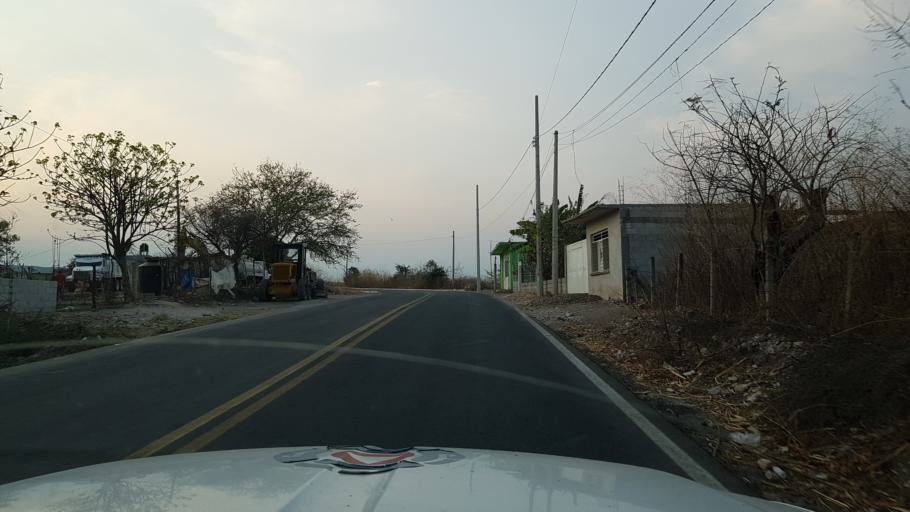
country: MX
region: Morelos
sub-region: Ayala
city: Olintepec
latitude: 18.7323
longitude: -99.0055
